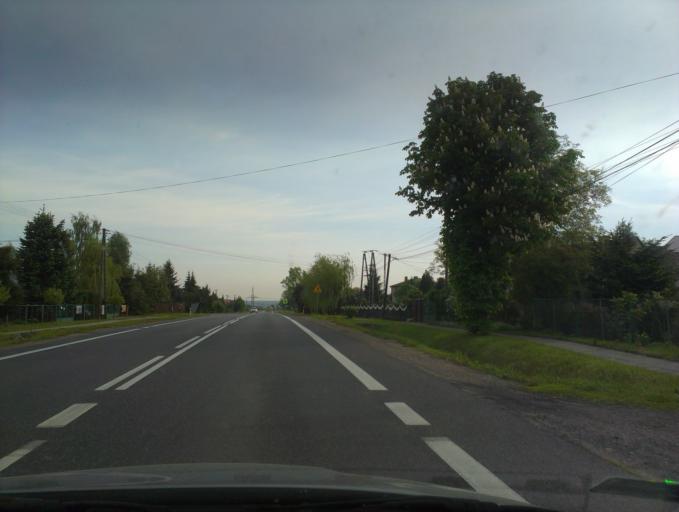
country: PL
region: Swietokrzyskie
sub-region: Powiat ostrowiecki
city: Ostrowiec Swietokrzyski
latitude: 50.9002
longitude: 21.3816
